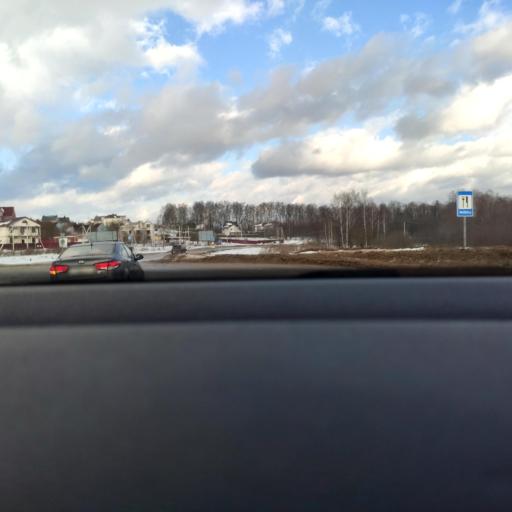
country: RU
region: Moskovskaya
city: Istra
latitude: 55.9809
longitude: 36.8109
